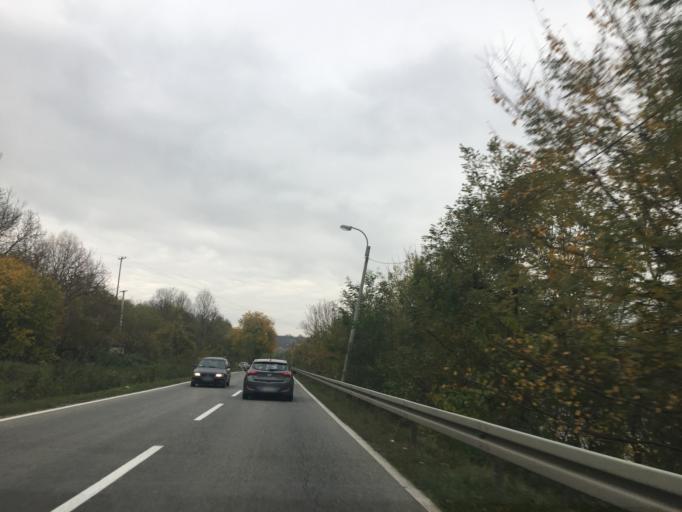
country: RS
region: Central Serbia
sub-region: Raski Okrug
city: Kraljevo
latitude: 43.7217
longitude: 20.7715
